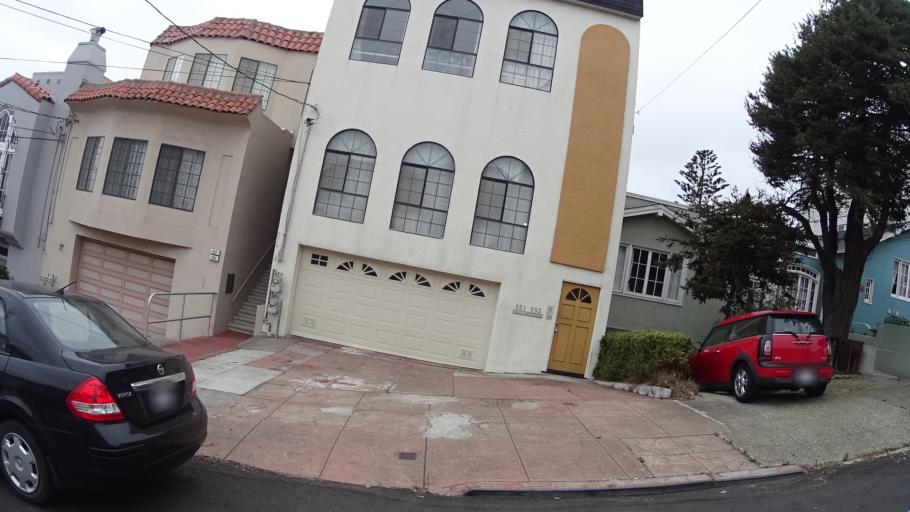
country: US
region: California
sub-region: Marin County
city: Sausalito
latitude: 37.7783
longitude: -122.5040
